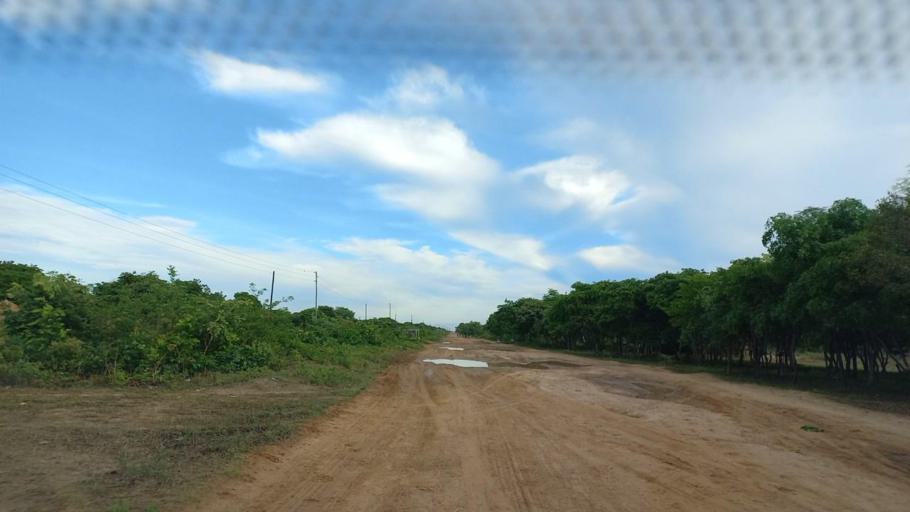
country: ZM
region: North-Western
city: Kabompo
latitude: -13.4272
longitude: 24.3268
